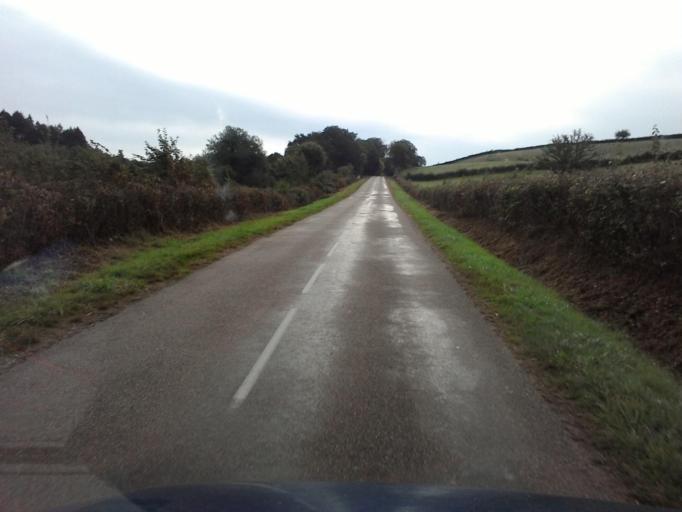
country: FR
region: Bourgogne
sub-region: Departement de la Nievre
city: Lormes
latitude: 47.2269
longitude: 3.8288
